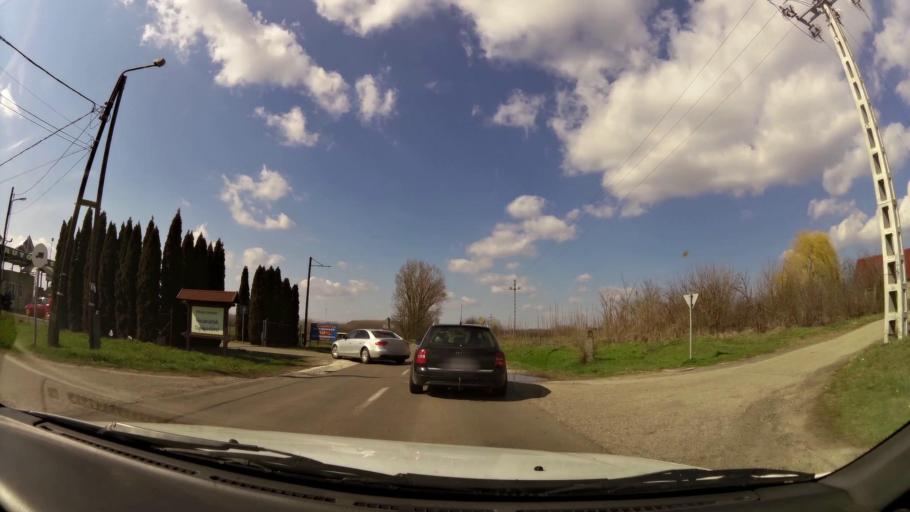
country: HU
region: Pest
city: Tapioszele
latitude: 47.3410
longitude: 19.8671
